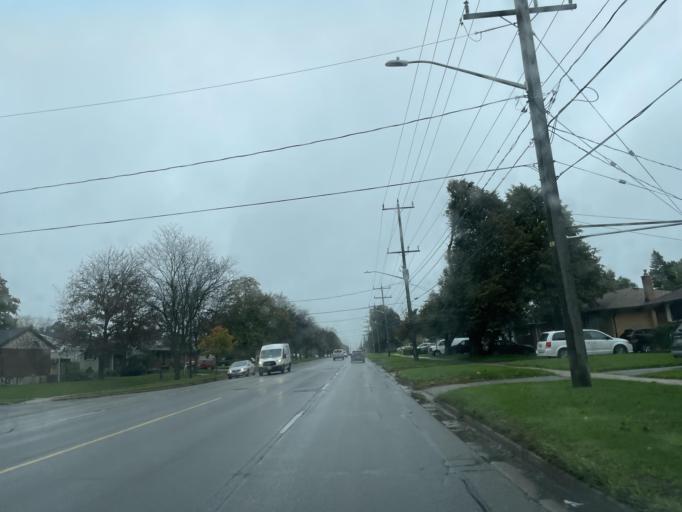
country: CA
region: Ontario
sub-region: Wellington County
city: Guelph
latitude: 43.5741
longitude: -80.2550
